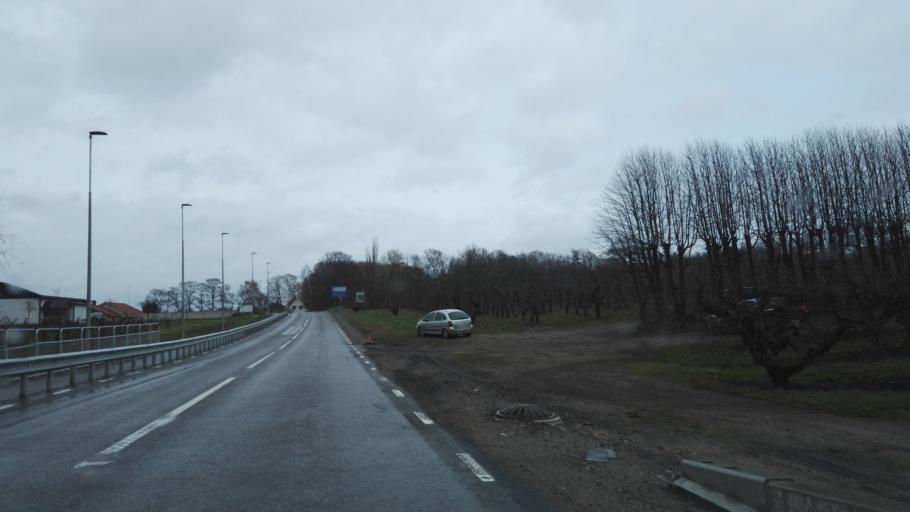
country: SE
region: Skane
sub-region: Simrishamns Kommun
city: Kivik
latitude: 55.6746
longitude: 14.2245
